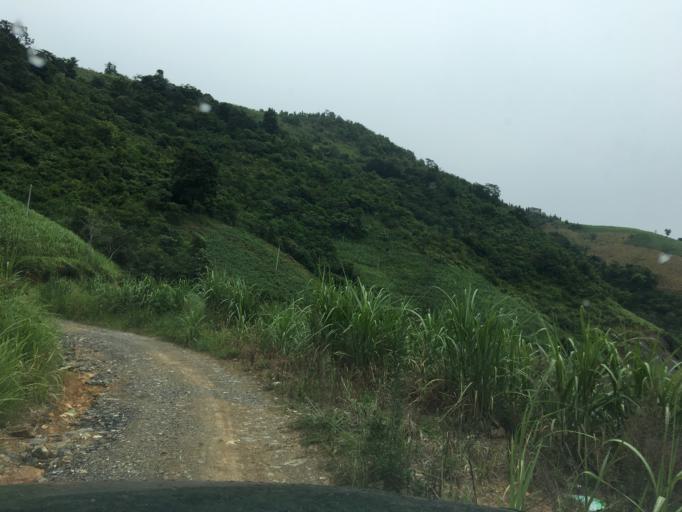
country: CN
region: Guangxi Zhuangzu Zizhiqu
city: Tongle
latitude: 25.0041
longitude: 105.9871
